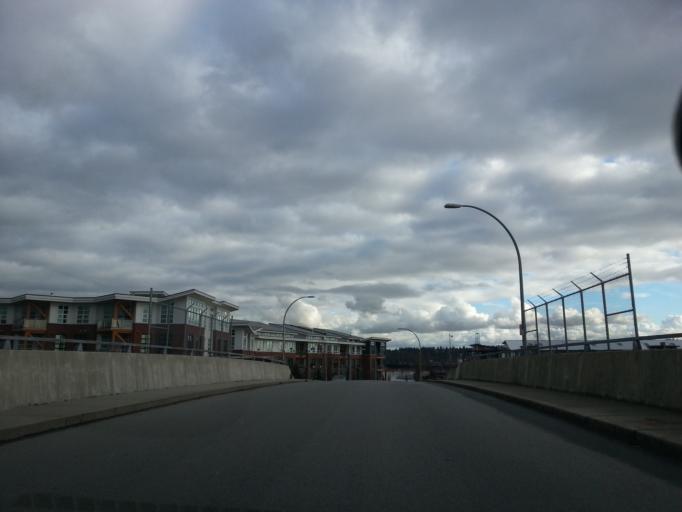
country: CA
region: British Columbia
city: New Westminster
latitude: 49.1957
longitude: -122.9248
